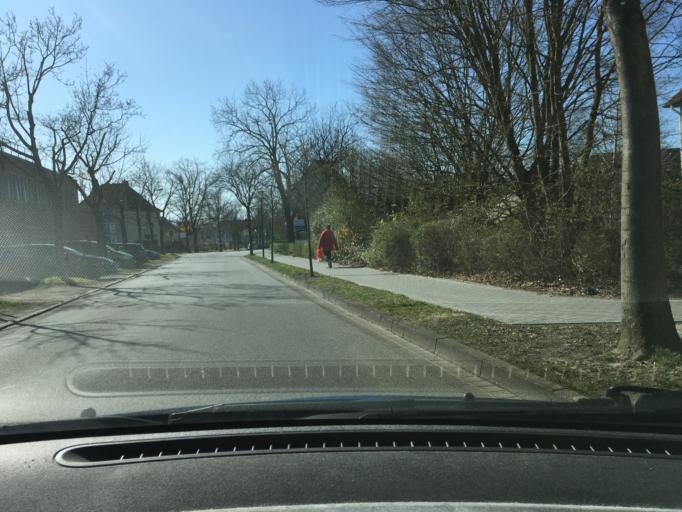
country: DE
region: Lower Saxony
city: Uelzen
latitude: 52.9714
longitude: 10.5481
